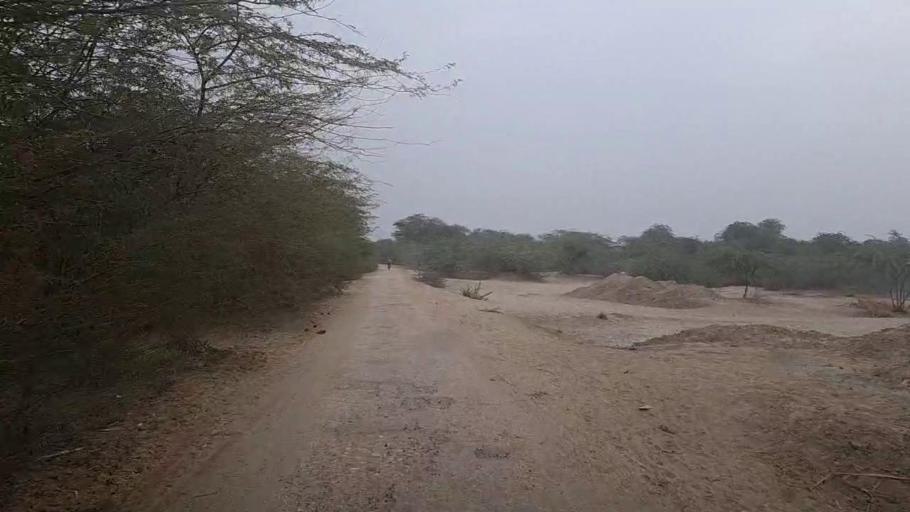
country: PK
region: Sindh
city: Gambat
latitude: 27.3536
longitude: 68.5993
